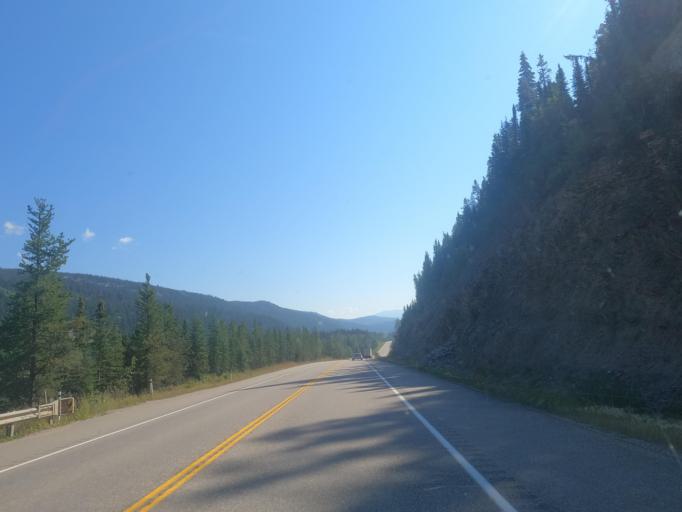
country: CA
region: Alberta
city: Jasper Park Lodge
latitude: 52.8769
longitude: -118.3339
